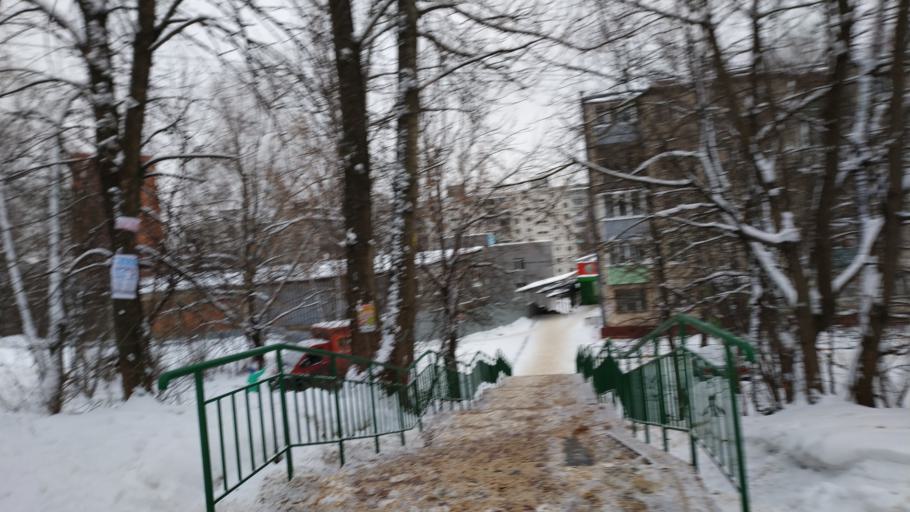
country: RU
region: Moskovskaya
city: Shchelkovo
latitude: 55.9302
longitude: 37.9933
